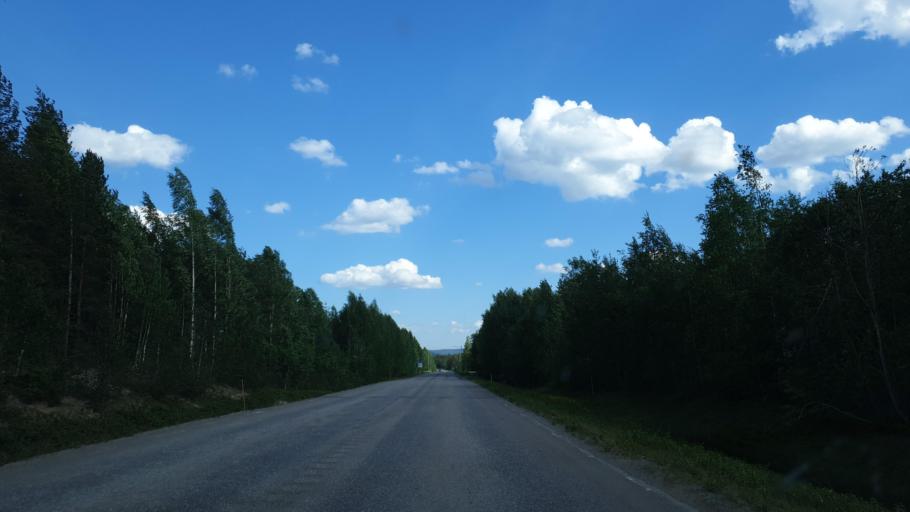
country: SE
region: Norrbotten
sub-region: Alvsbyns Kommun
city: AElvsbyn
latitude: 65.8410
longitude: 20.5036
